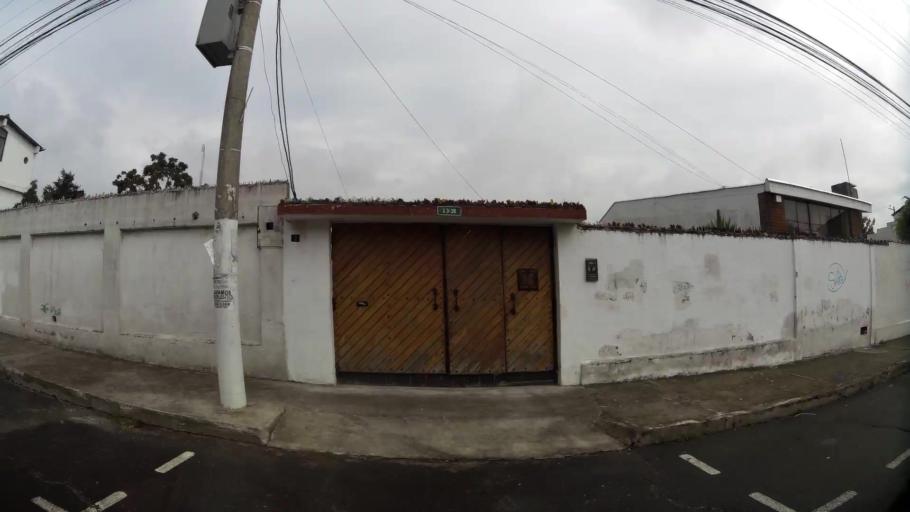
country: EC
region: Pichincha
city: Sangolqui
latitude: -0.2952
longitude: -78.4781
